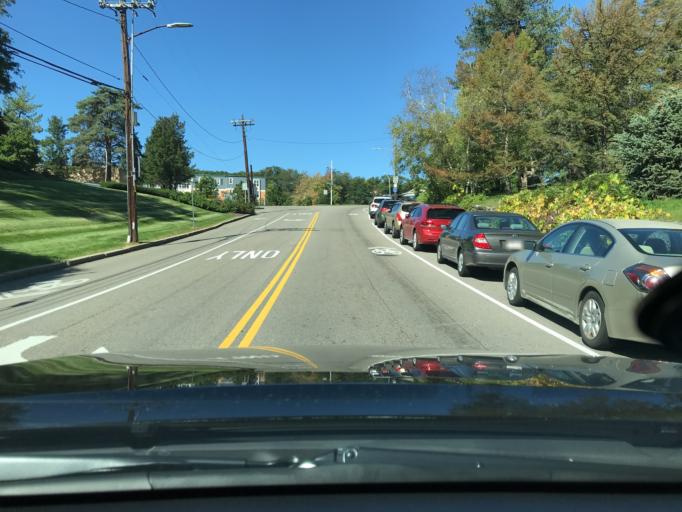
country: US
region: Massachusetts
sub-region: Suffolk County
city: Jamaica Plain
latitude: 42.2970
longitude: -71.1295
